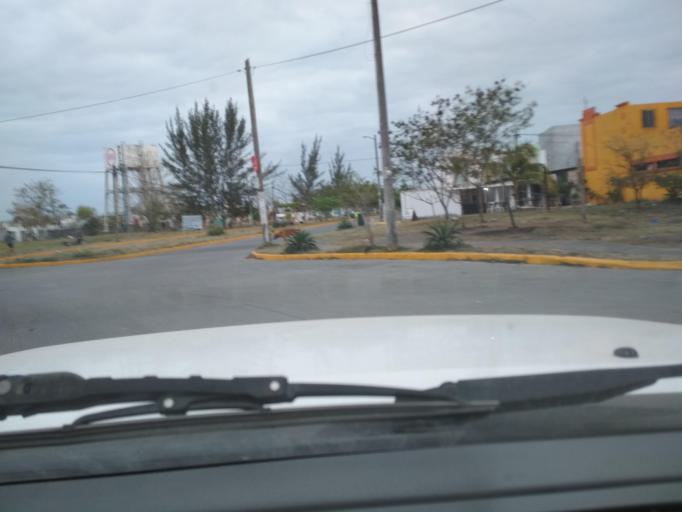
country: MX
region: Veracruz
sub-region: Medellin
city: Fraccionamiento Arboledas San Ramon
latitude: 19.0936
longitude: -96.1552
